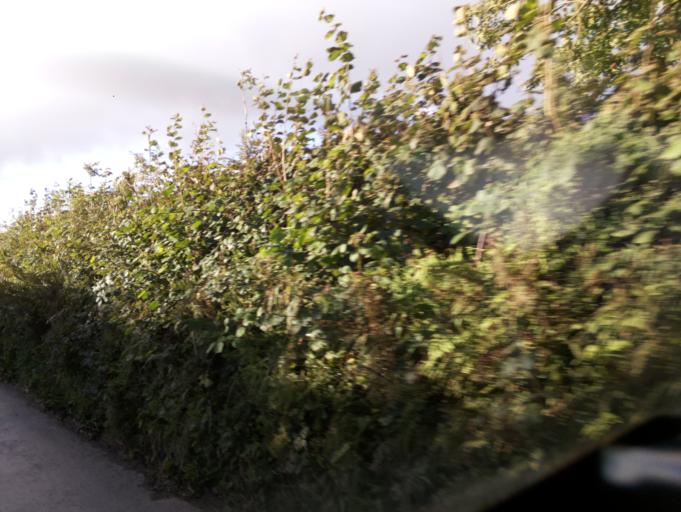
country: GB
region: England
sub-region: Devon
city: Totnes
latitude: 50.3632
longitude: -3.7370
